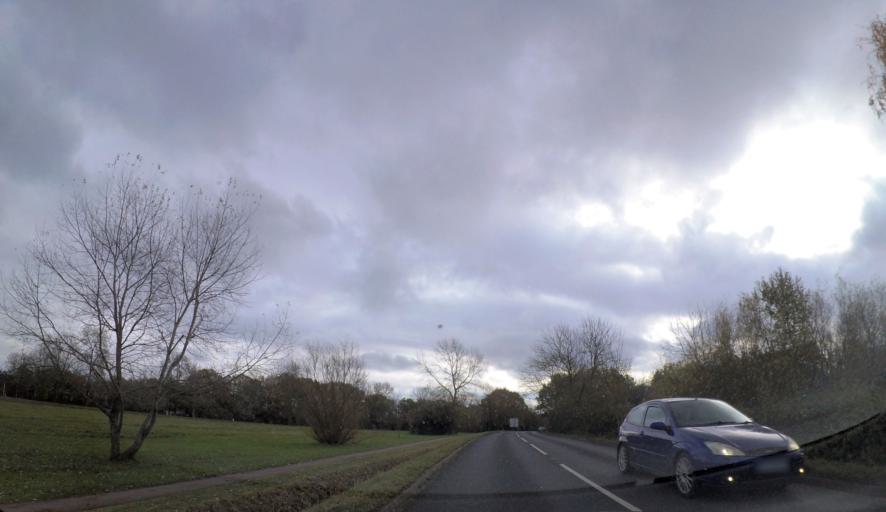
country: GB
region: England
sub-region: Surrey
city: Salfords
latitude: 51.2102
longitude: -0.1712
